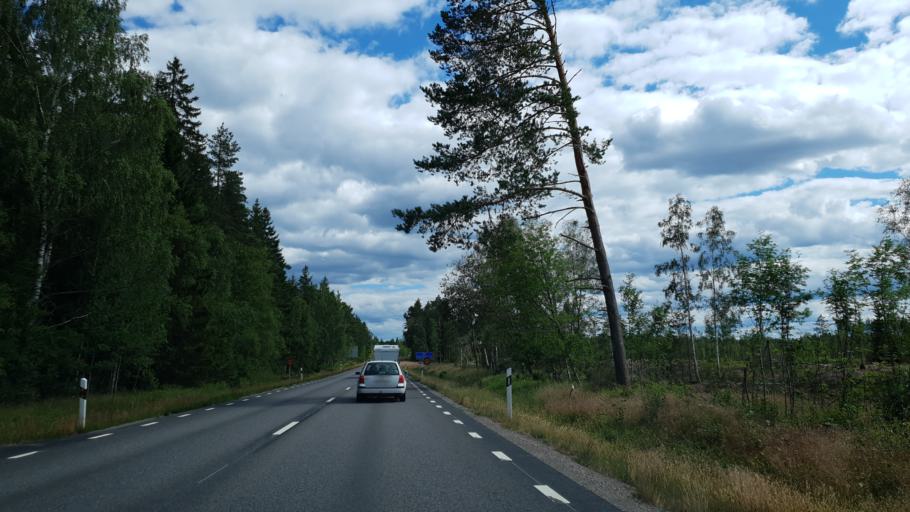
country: SE
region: Kronoberg
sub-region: Lessebo Kommun
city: Lessebo
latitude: 56.8305
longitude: 15.3977
